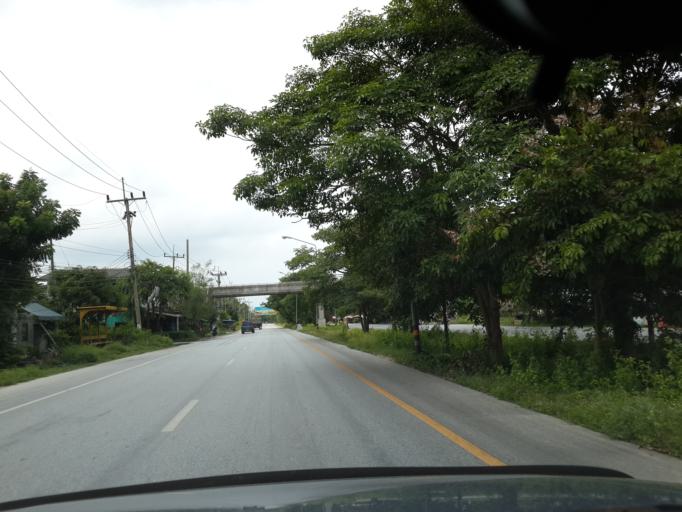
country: TH
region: Pattani
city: Yaring
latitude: 6.8695
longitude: 101.3214
